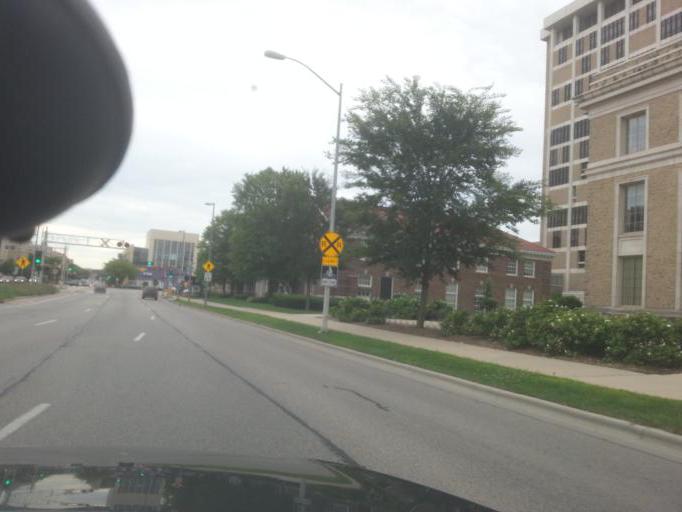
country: US
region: Wisconsin
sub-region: Dane County
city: Madison
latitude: 43.0734
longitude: -89.4123
